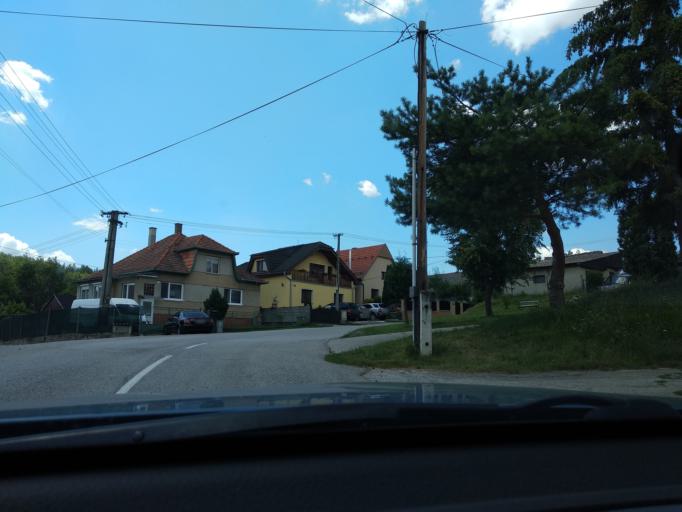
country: SK
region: Nitriansky
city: Banovce nad Bebravou
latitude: 48.7028
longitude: 18.1928
